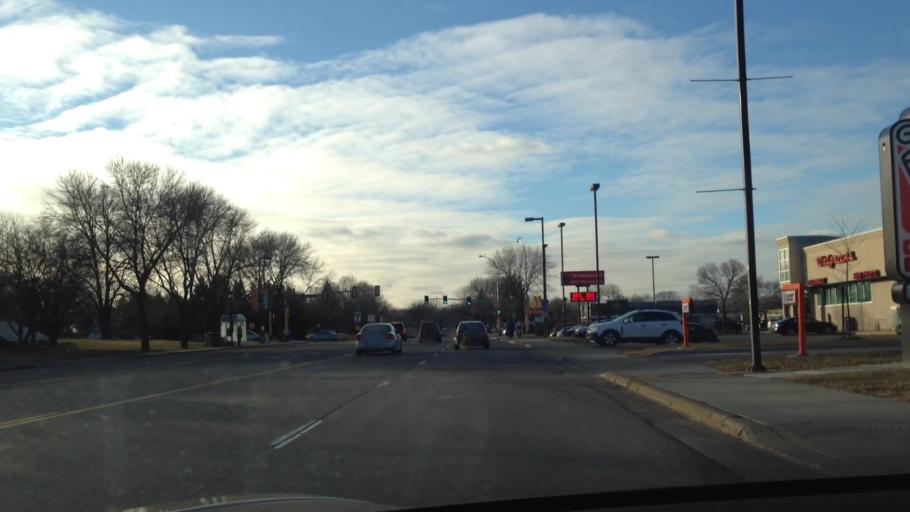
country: US
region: Minnesota
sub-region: Hennepin County
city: New Hope
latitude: 45.0329
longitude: -93.3786
